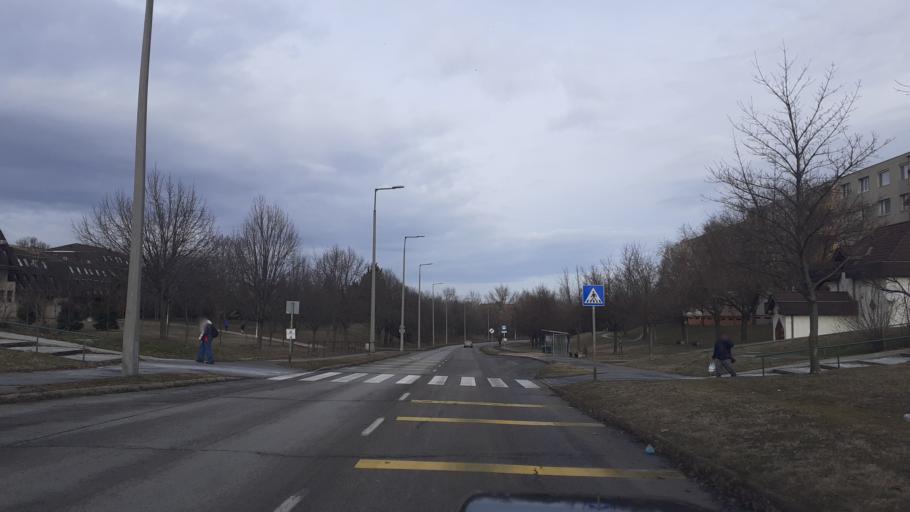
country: HU
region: Fejer
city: dunaujvaros
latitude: 46.9664
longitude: 18.9160
